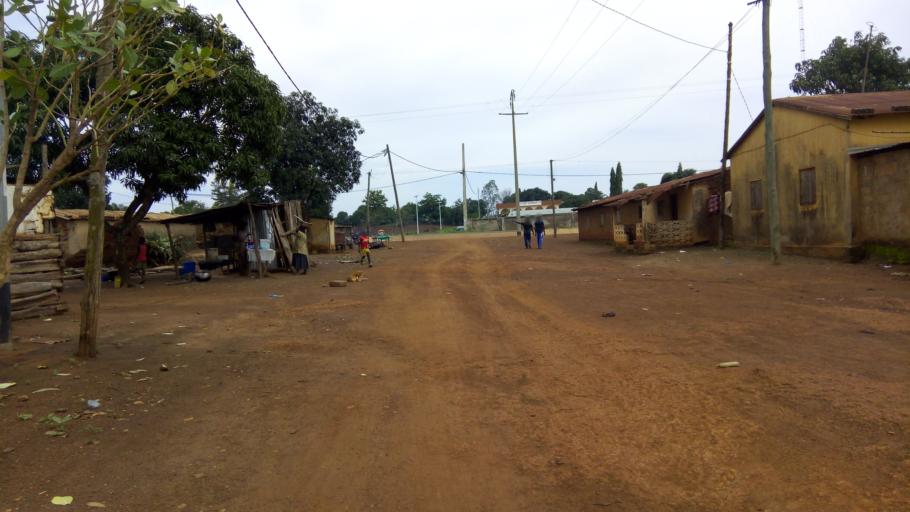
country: TG
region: Centrale
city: Sotouboua
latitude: 8.5662
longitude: 0.9801
